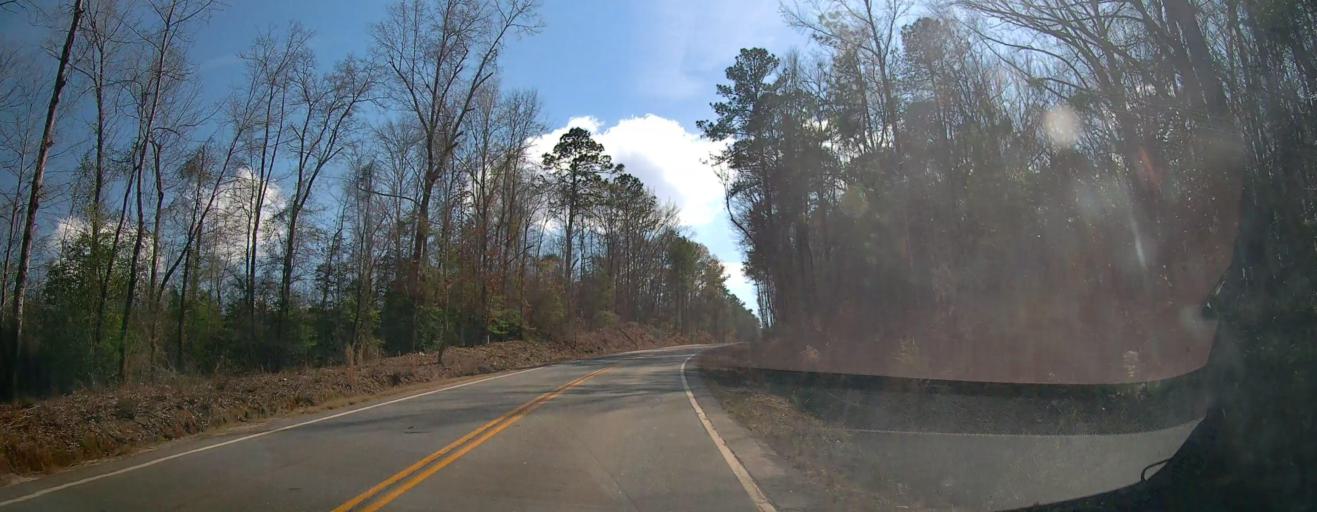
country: US
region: Georgia
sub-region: Wilkinson County
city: Gordon
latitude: 32.8107
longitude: -83.3240
